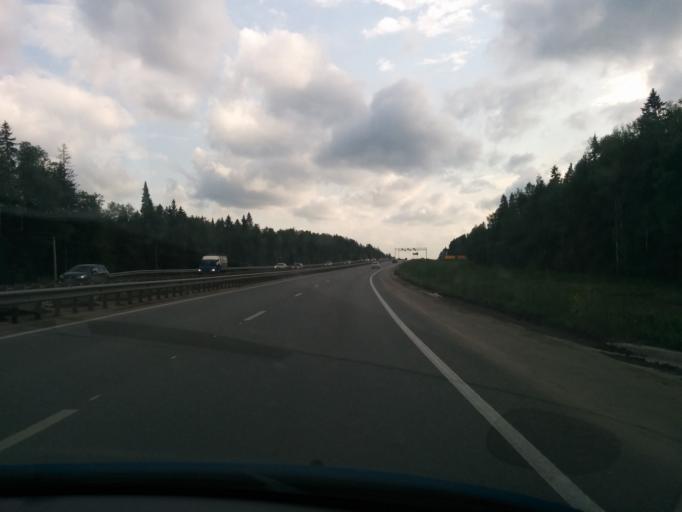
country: RU
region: Perm
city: Ferma
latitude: 58.0297
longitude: 56.4317
